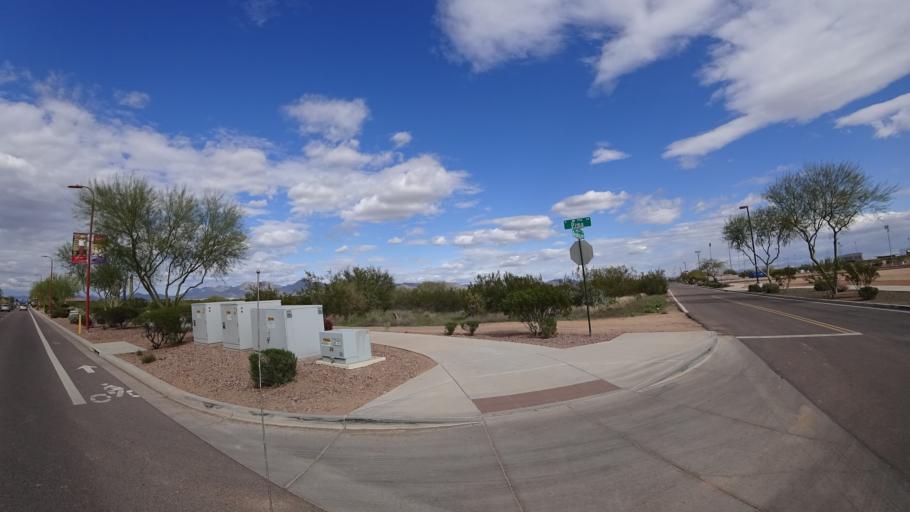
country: US
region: Arizona
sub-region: Maricopa County
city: Scottsdale
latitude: 33.5491
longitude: -111.8914
